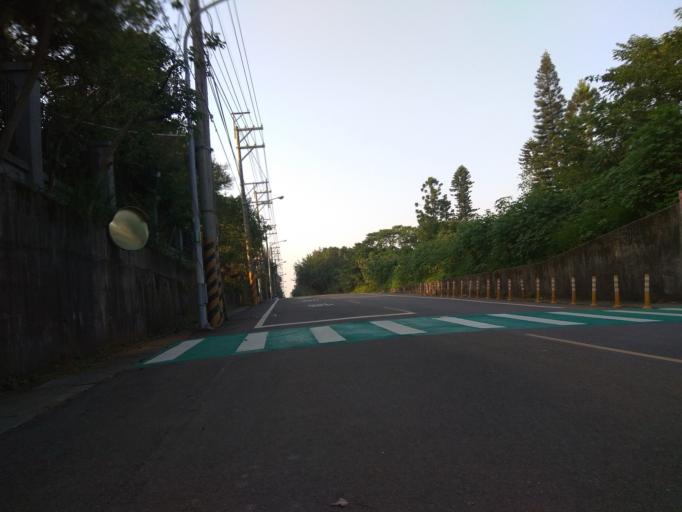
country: TW
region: Taiwan
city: Daxi
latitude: 24.9248
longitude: 121.1825
